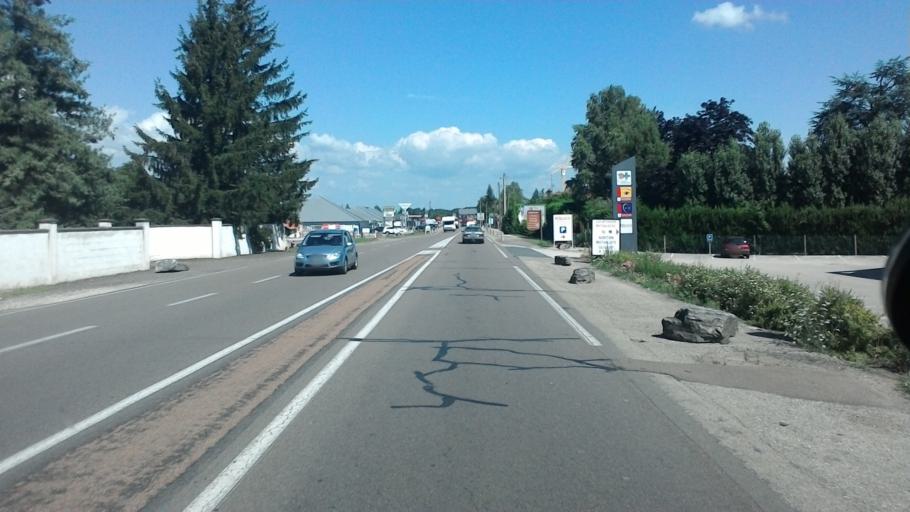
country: FR
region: Bourgogne
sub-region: Departement de Saone-et-Loire
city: Sevrey
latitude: 46.7505
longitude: 4.8492
